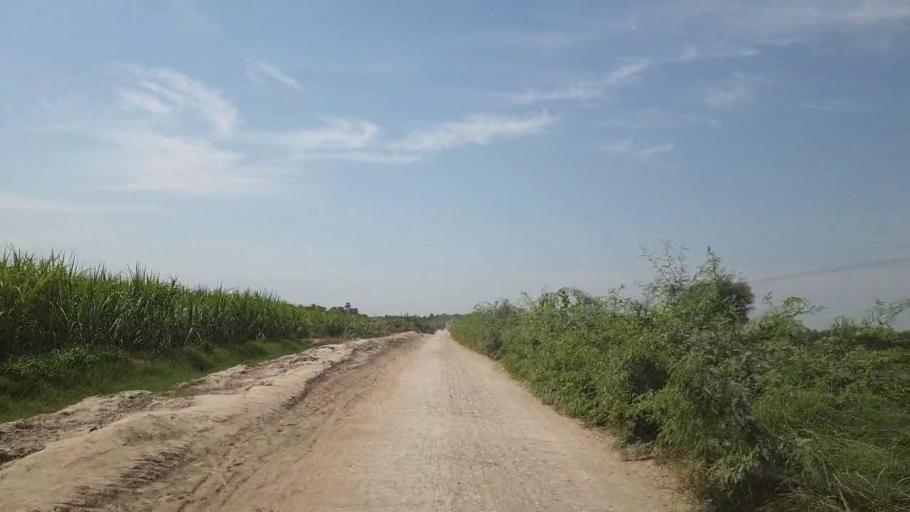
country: PK
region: Sindh
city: Tando Jam
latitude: 25.3991
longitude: 68.5949
